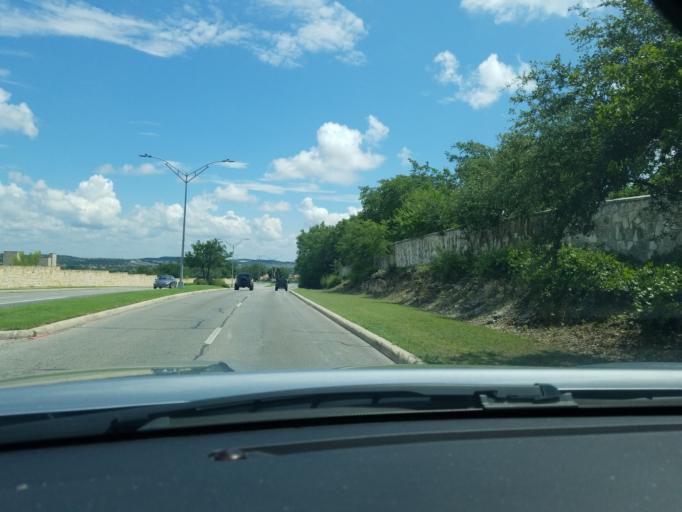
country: US
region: Texas
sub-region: Bexar County
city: Timberwood Park
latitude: 29.6575
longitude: -98.4804
